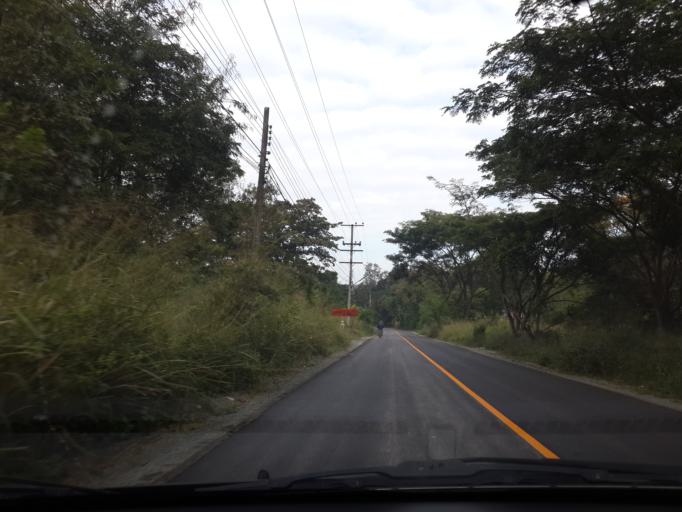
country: TH
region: Chiang Mai
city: San Sai
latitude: 18.9215
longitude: 99.1307
